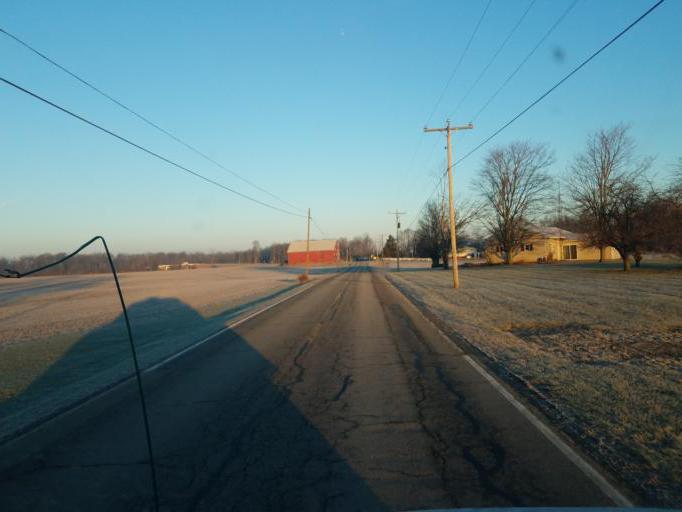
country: US
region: Ohio
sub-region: Marion County
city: Marion
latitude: 40.5314
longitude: -83.0682
